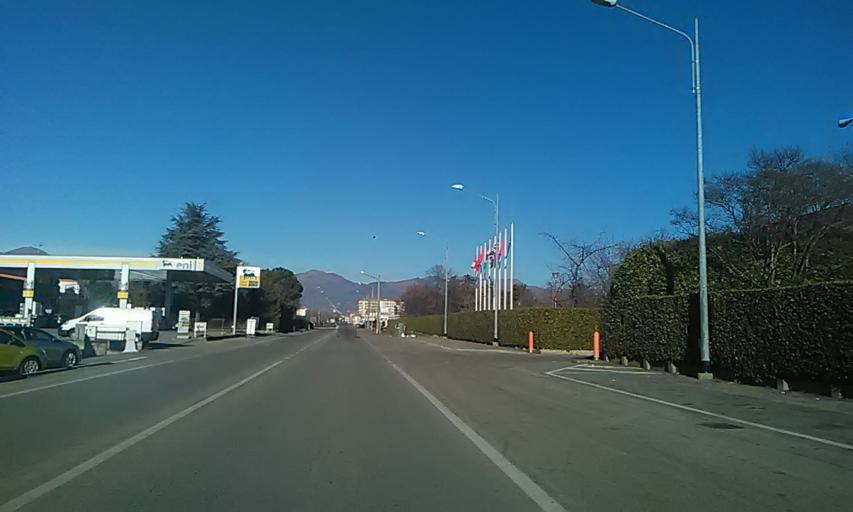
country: IT
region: Piedmont
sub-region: Provincia di Biella
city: Sandigliano
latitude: 45.5267
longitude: 8.0751
